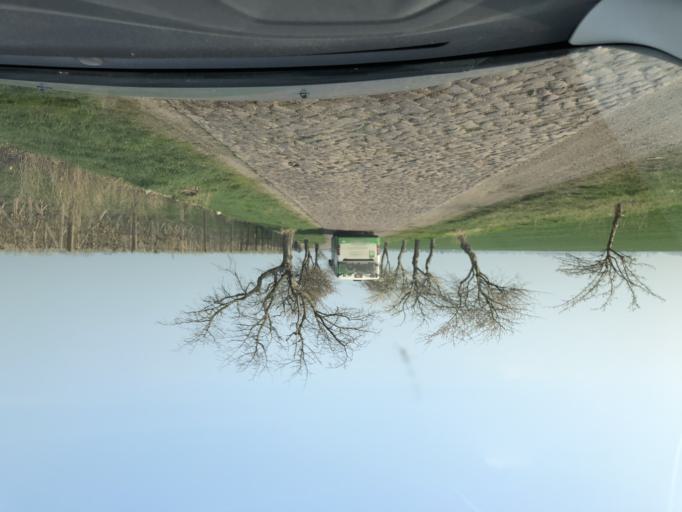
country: DE
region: Saxony-Anhalt
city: Zorbig
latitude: 51.6080
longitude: 12.1104
